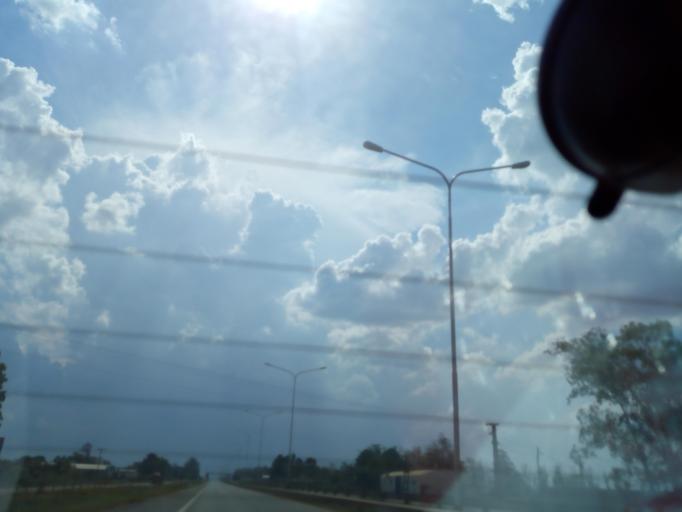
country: AR
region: Corrientes
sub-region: Departamento de Paso de los Libres
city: Paso de los Libres
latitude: -29.7220
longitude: -57.1338
